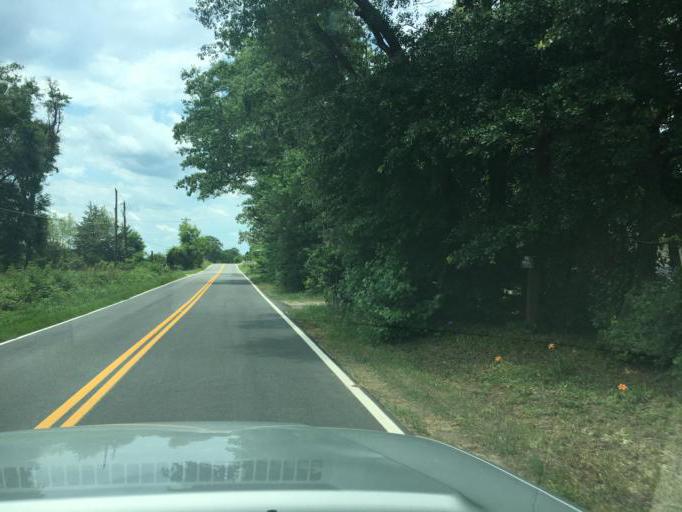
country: US
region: South Carolina
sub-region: Spartanburg County
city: Duncan
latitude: 34.8763
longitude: -82.1811
